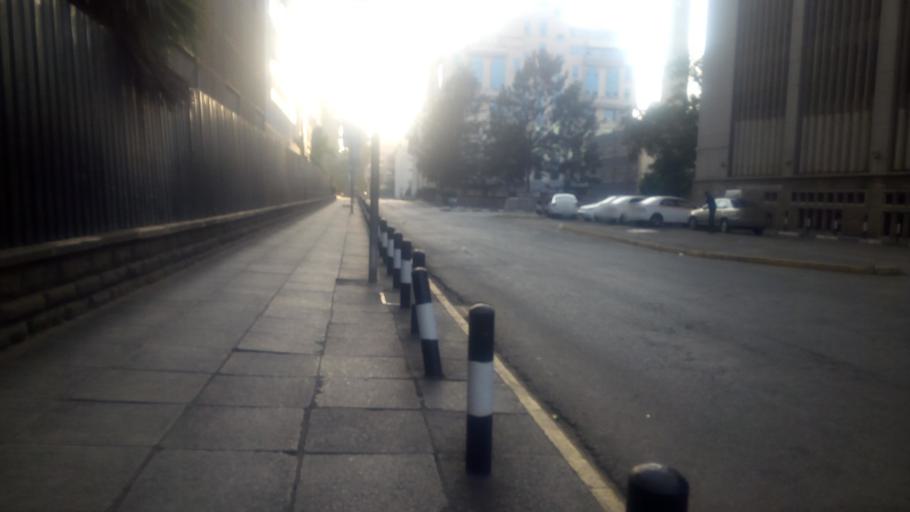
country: KE
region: Nairobi Area
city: Nairobi
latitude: -1.2873
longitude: 36.8188
